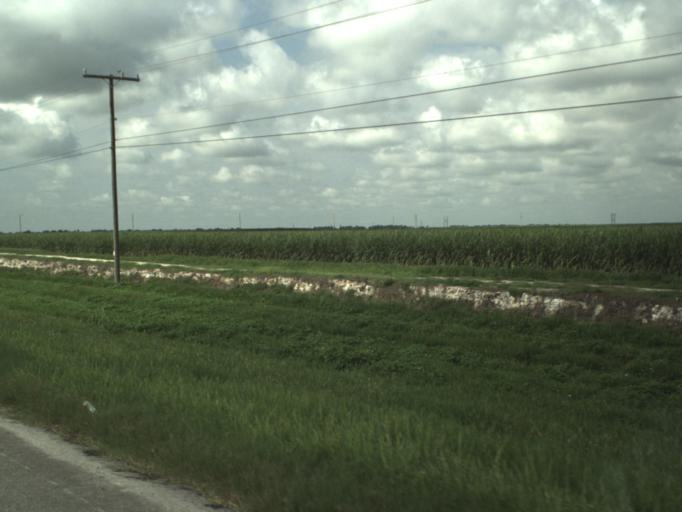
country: US
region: Florida
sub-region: Palm Beach County
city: Belle Glade
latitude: 26.7342
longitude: -80.6841
